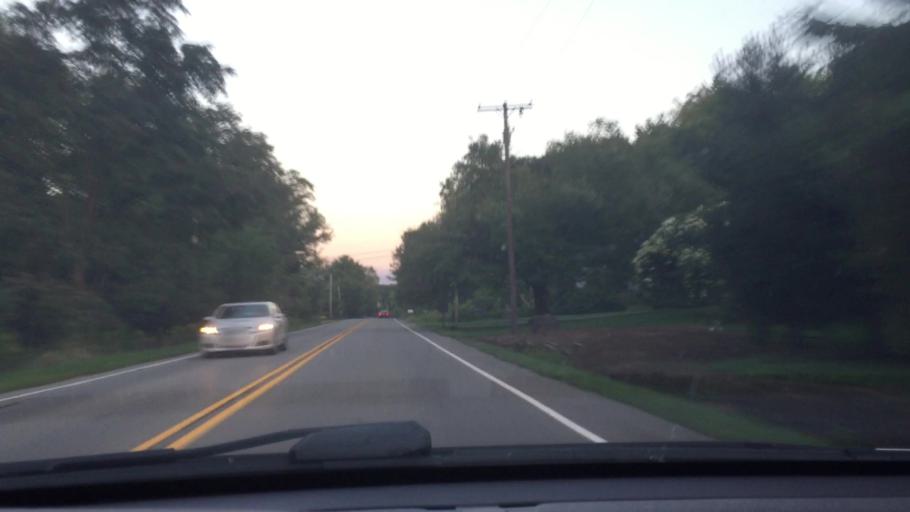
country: US
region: Pennsylvania
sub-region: Mercer County
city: Grove City
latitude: 41.1234
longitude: -80.0662
